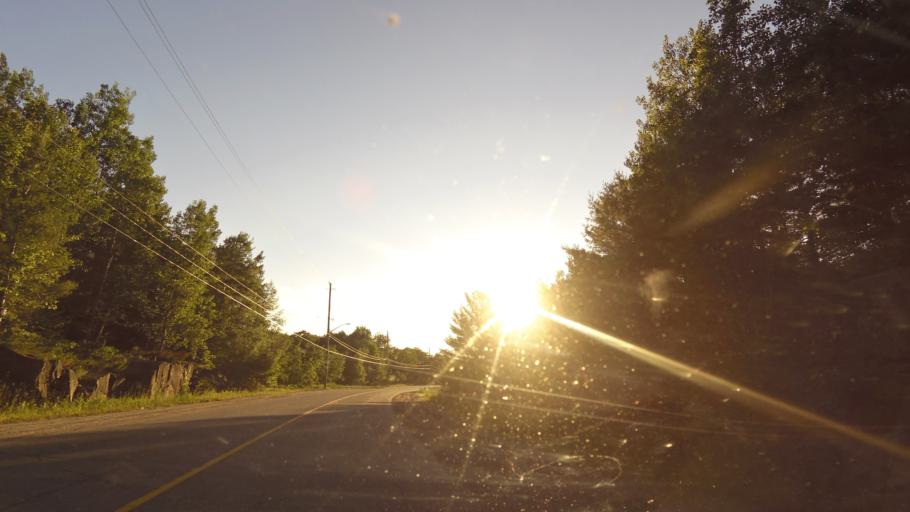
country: CA
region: Ontario
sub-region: Parry Sound District
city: Parry Sound
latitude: 45.3598
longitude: -80.0359
